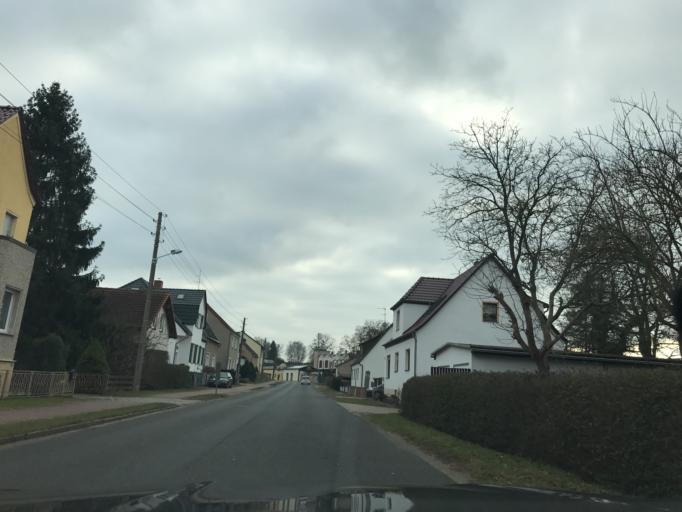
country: DE
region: Brandenburg
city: Brandenburg an der Havel
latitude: 52.3701
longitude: 12.5470
